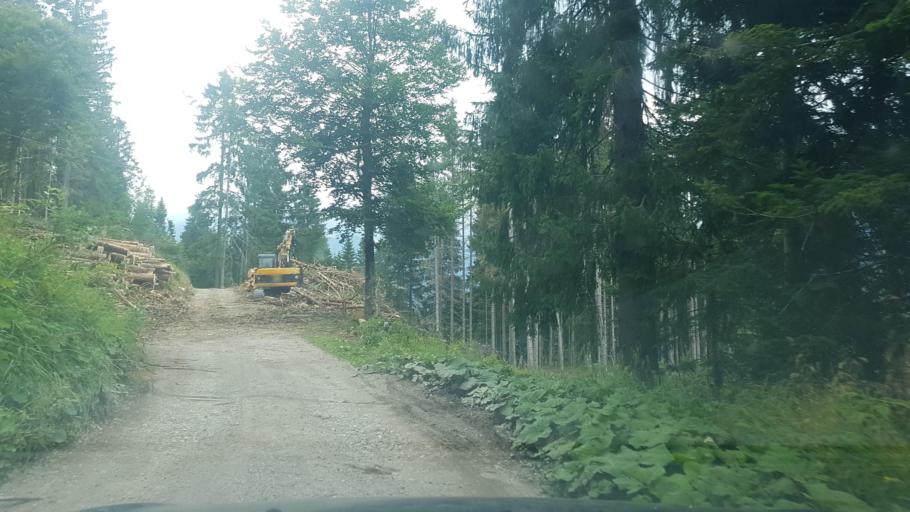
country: IT
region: Friuli Venezia Giulia
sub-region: Provincia di Udine
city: Rigolato
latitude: 46.5600
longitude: 12.8122
